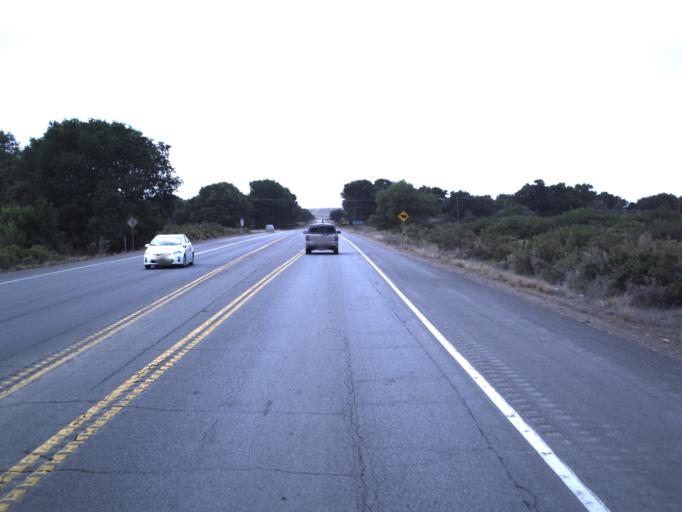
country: US
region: Utah
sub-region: Duchesne County
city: Duchesne
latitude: 40.1543
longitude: -110.2151
